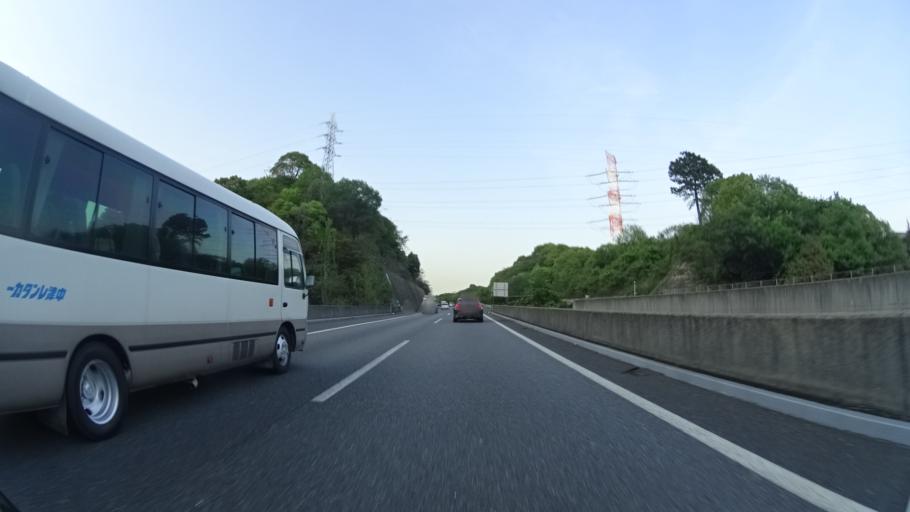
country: JP
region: Okayama
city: Kurashiki
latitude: 34.4844
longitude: 133.7843
